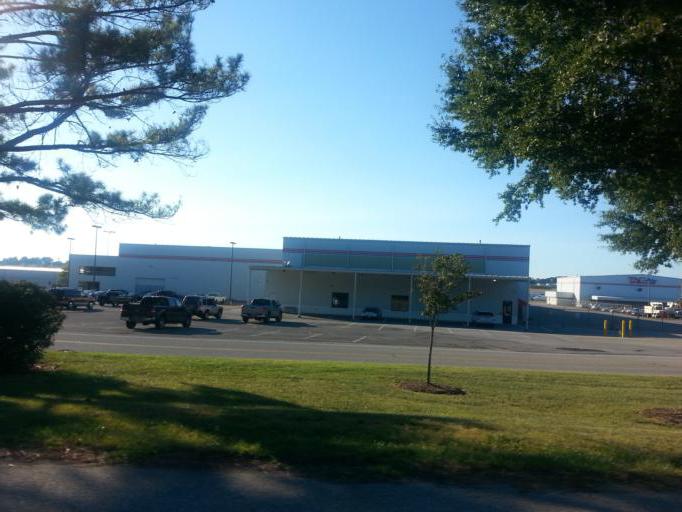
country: US
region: Tennessee
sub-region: Blount County
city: Alcoa
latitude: 35.8091
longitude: -83.9852
